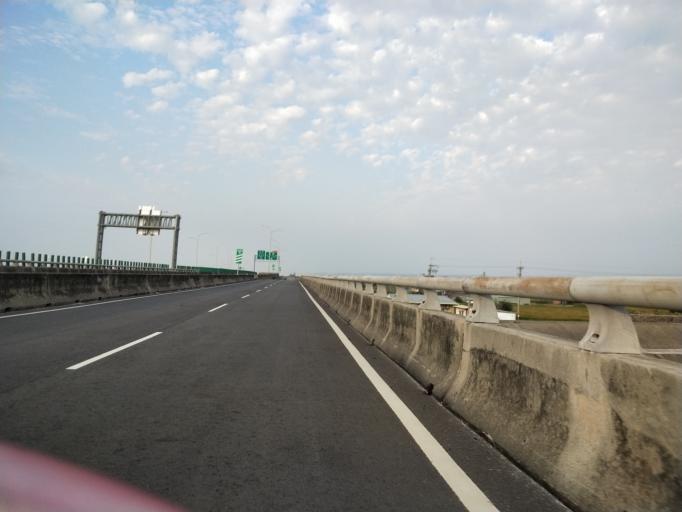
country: TW
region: Taiwan
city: Fengyuan
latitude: 24.4026
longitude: 120.6117
